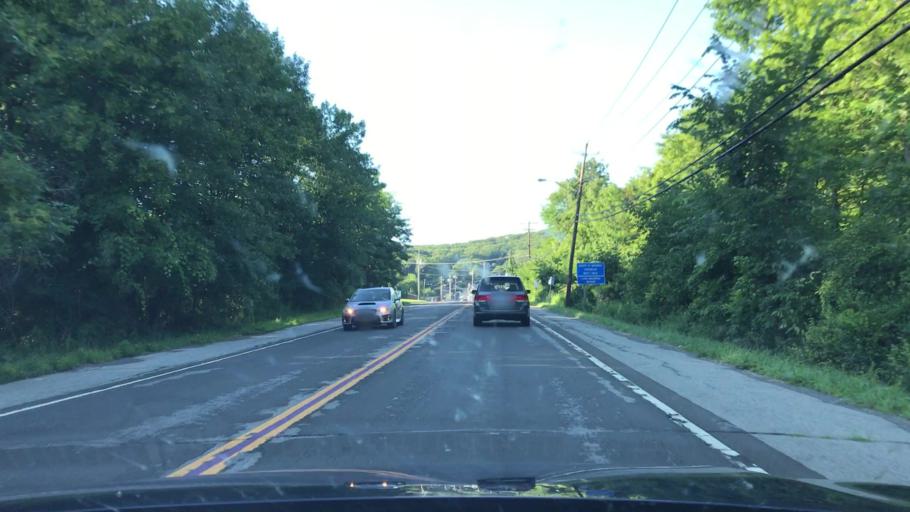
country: US
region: New York
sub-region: Putnam County
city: Mahopac
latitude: 41.3564
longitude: -73.7470
